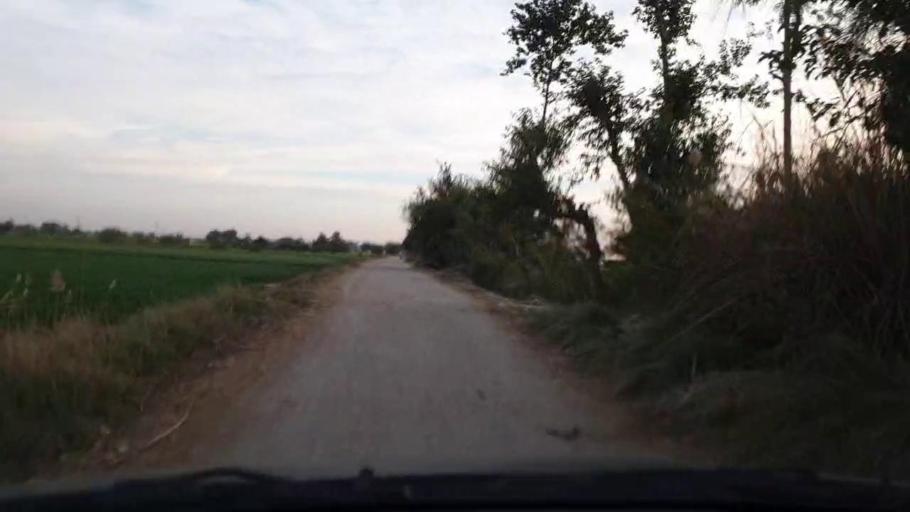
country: PK
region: Sindh
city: Khadro
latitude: 26.1247
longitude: 68.7780
